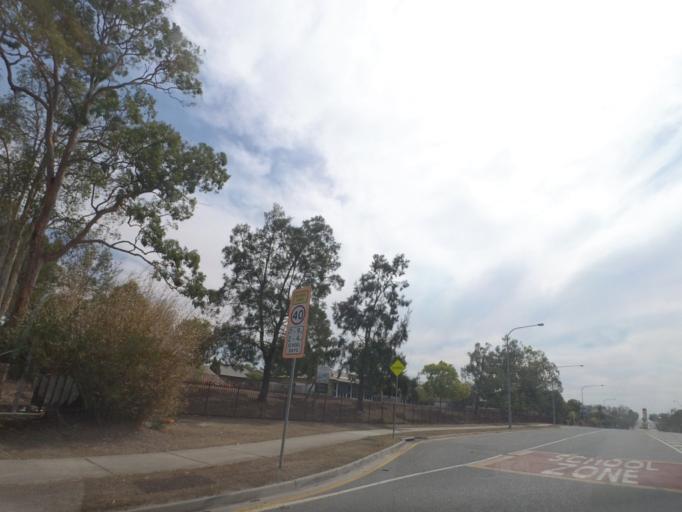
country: AU
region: Queensland
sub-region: Brisbane
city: Sunnybank Hills
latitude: -27.6401
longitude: 153.0568
